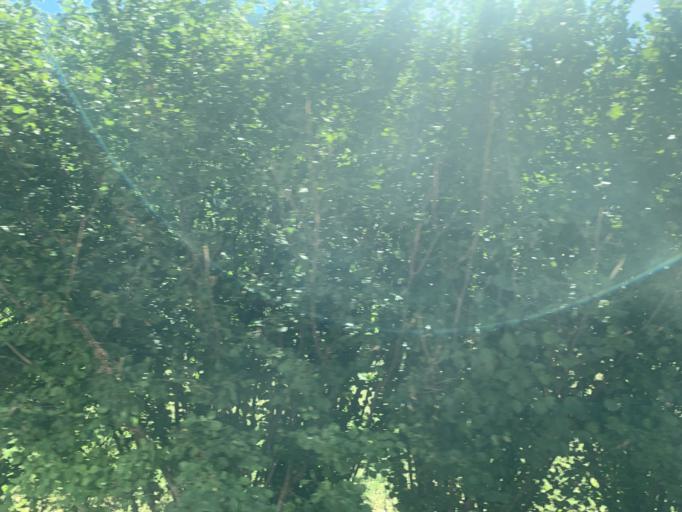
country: ES
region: Aragon
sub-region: Provincia de Huesca
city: Broto
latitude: 42.6358
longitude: -0.1117
